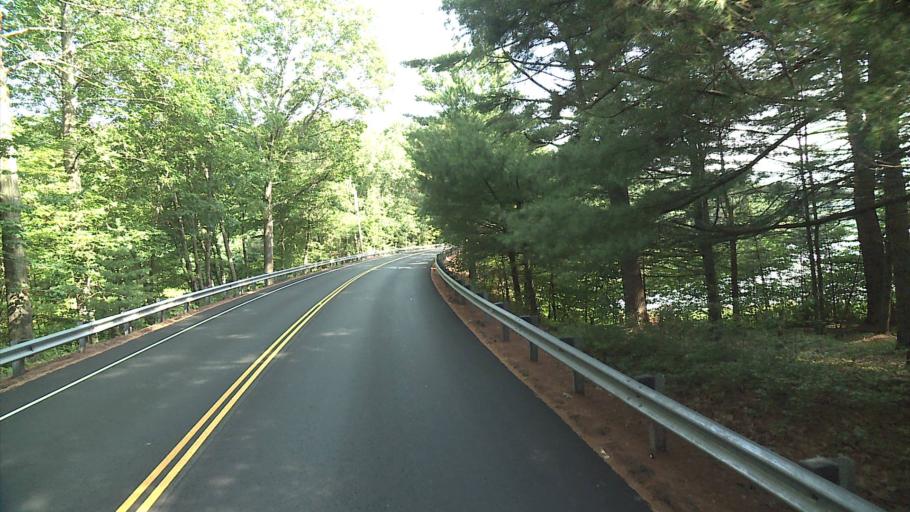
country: US
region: Connecticut
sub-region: New Haven County
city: Ansonia
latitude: 41.3702
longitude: -73.0618
